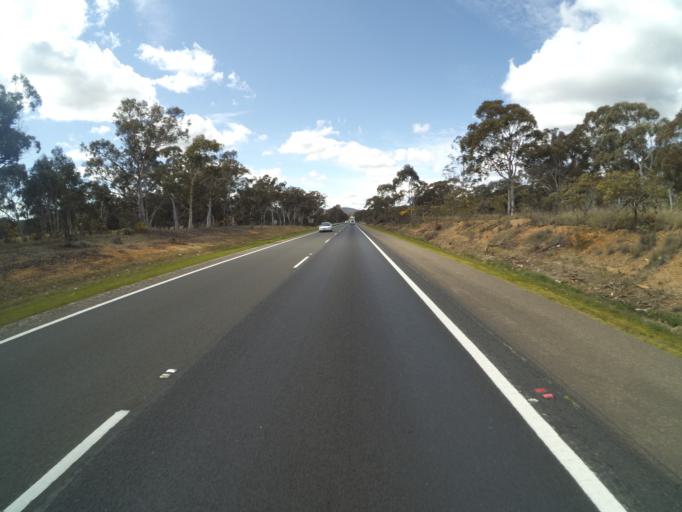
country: AU
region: New South Wales
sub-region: Goulburn Mulwaree
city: Goulburn
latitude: -34.7447
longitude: 149.8821
